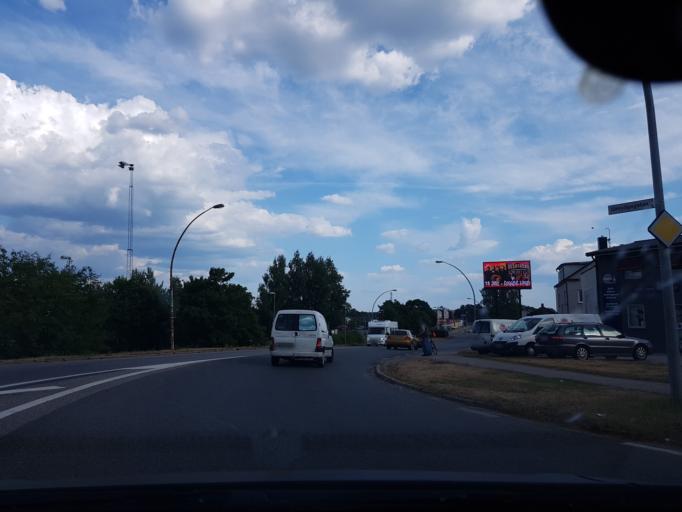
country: SE
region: Joenkoeping
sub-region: Gislaveds Kommun
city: Gislaved
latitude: 57.3057
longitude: 13.5410
